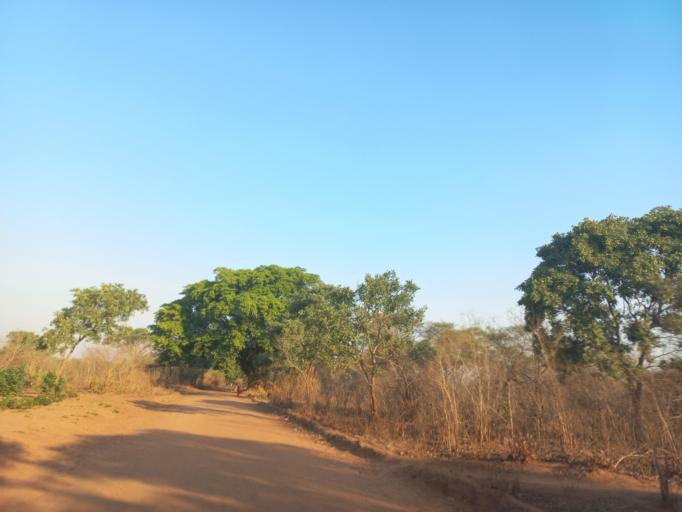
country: ZM
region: Lusaka
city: Luangwa
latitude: -15.4353
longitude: 30.3500
